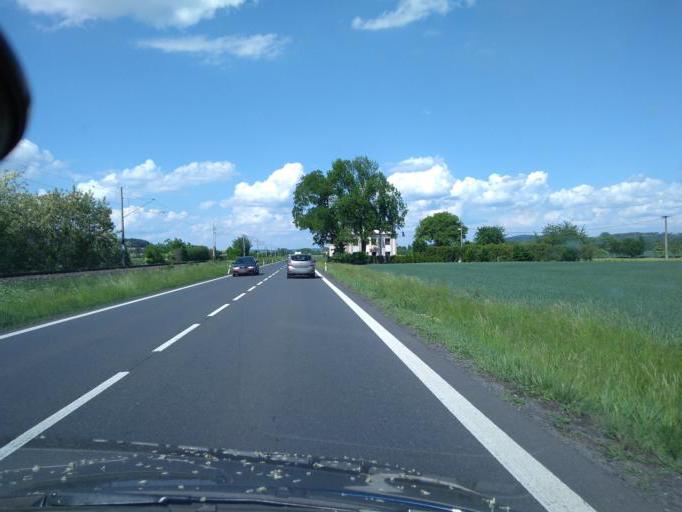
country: CZ
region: Plzensky
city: Prestice
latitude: 49.5382
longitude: 13.3077
